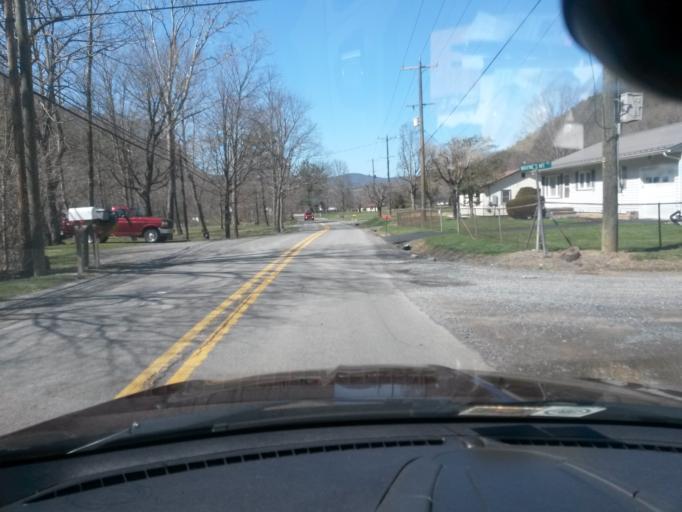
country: US
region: West Virginia
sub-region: Greenbrier County
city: White Sulphur Springs
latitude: 37.7815
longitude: -80.2845
